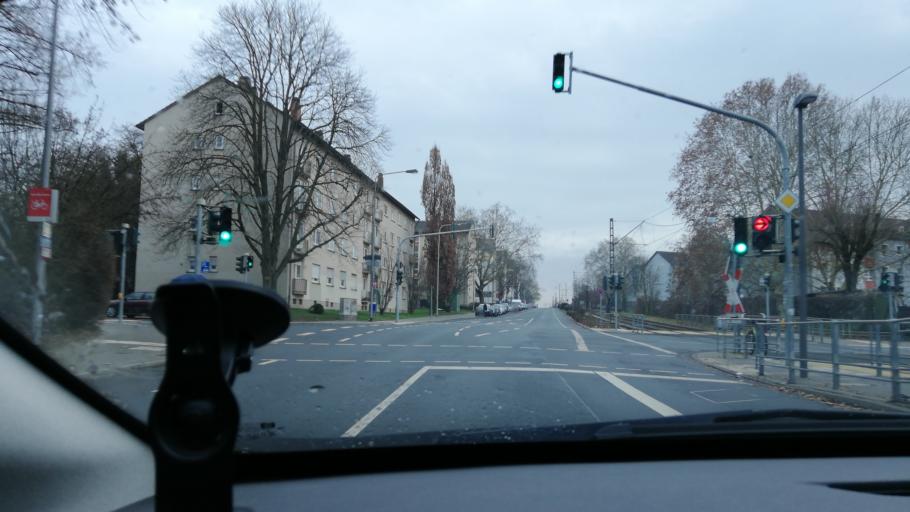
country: DE
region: Hesse
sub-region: Regierungsbezirk Darmstadt
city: Frankfurt am Main
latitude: 50.1511
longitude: 8.6884
